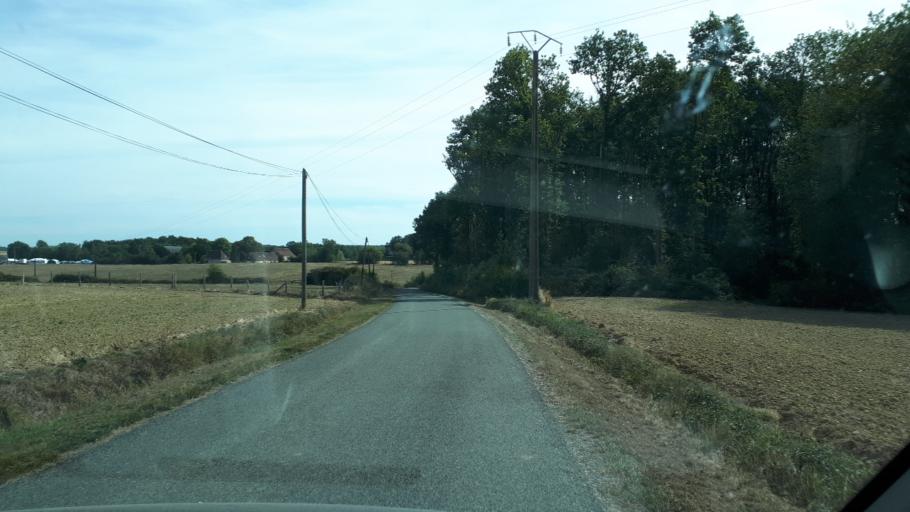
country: FR
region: Centre
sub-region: Departement du Loir-et-Cher
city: Montoire-sur-le-Loir
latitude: 47.6956
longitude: 0.8406
